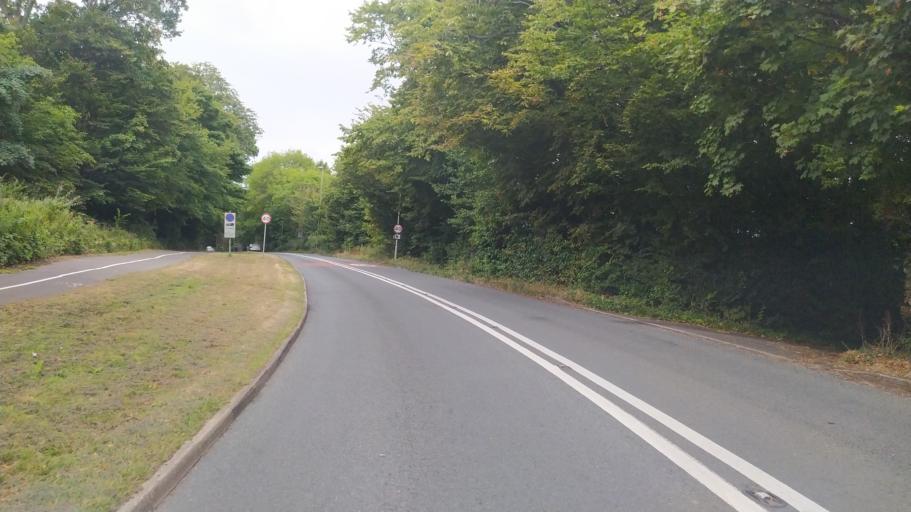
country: GB
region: England
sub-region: Hampshire
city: Havant
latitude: 50.8780
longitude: -0.9713
